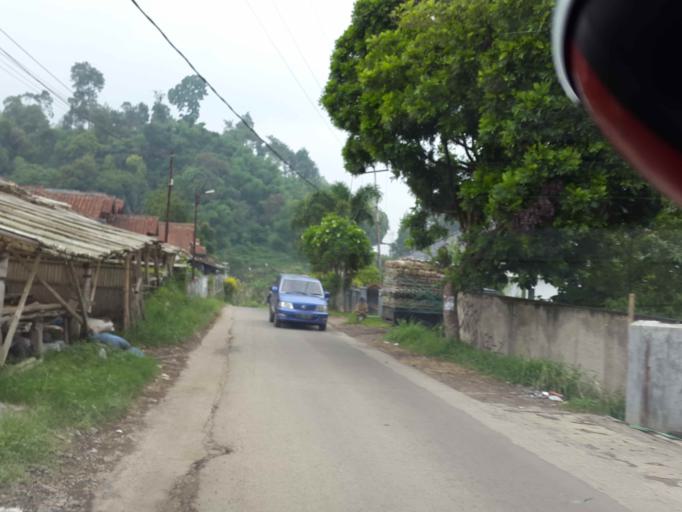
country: ID
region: West Java
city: Lembang
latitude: -6.8166
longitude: 107.5878
